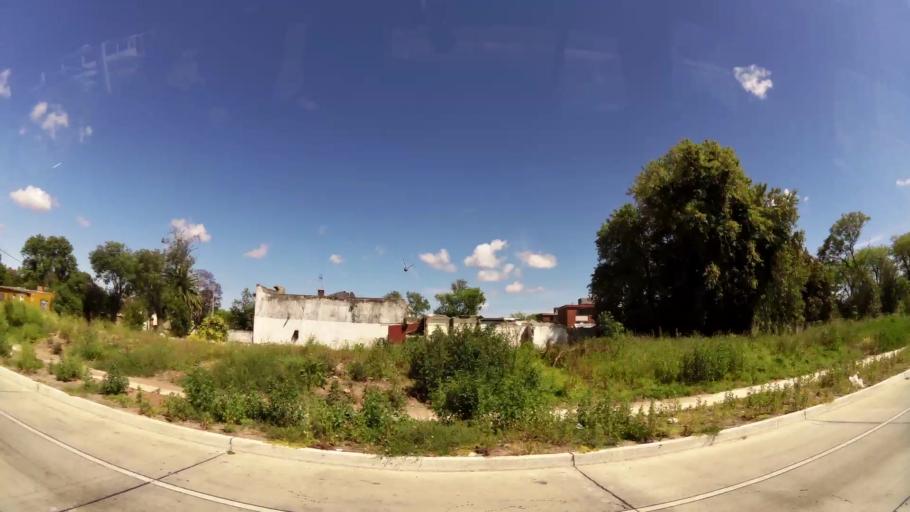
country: UY
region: Montevideo
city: Montevideo
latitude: -34.8466
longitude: -56.1462
